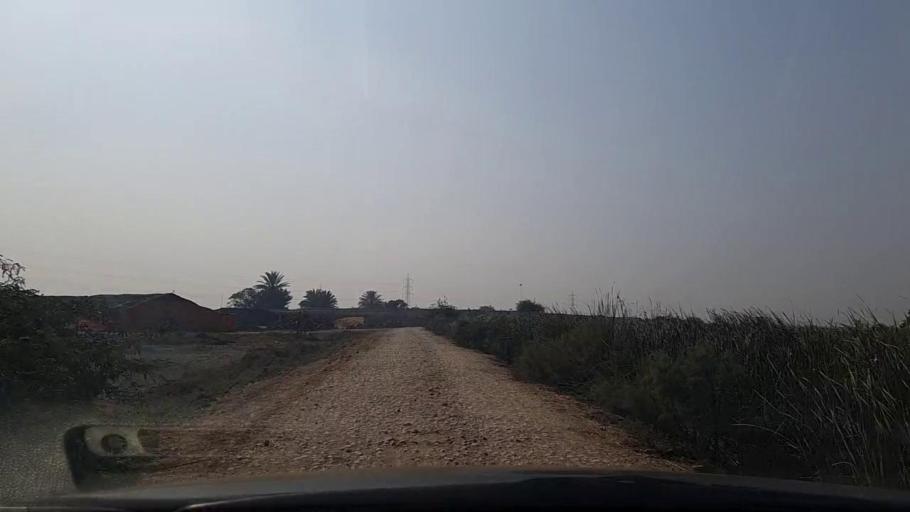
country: PK
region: Sindh
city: Mirpur Sakro
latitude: 24.5711
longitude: 67.7787
